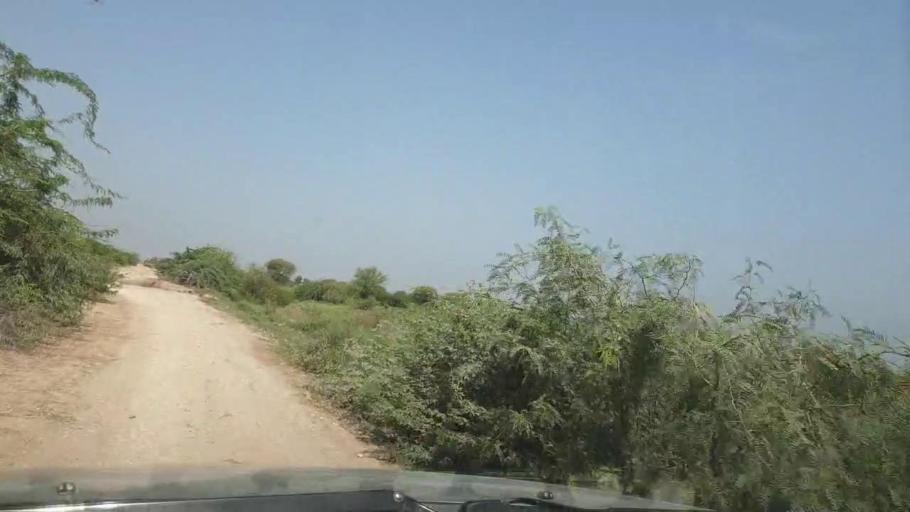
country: PK
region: Sindh
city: Tando Ghulam Ali
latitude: 25.0889
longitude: 68.8021
